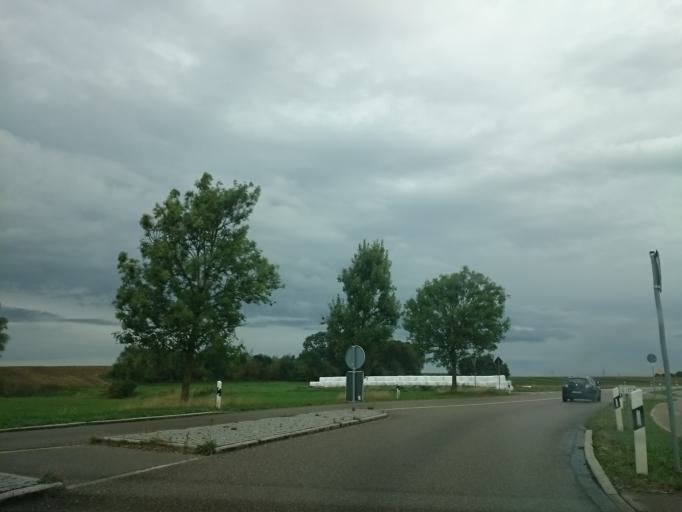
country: DE
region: Bavaria
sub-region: Swabia
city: Graben
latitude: 48.1988
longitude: 10.8259
